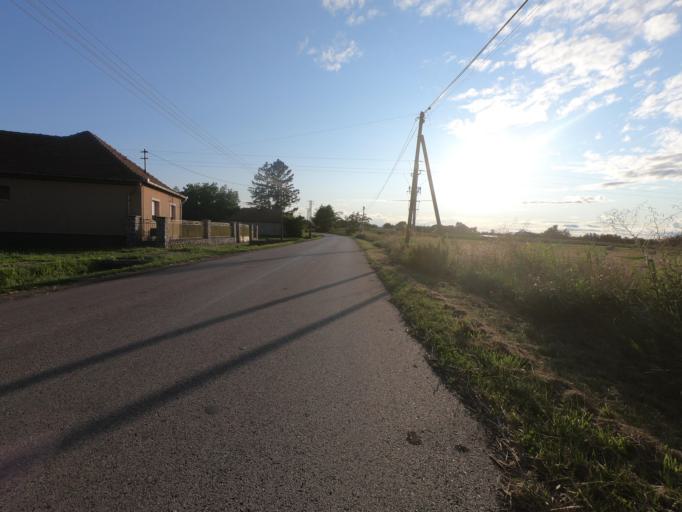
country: HU
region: Heves
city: Szihalom
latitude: 47.7157
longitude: 20.5275
